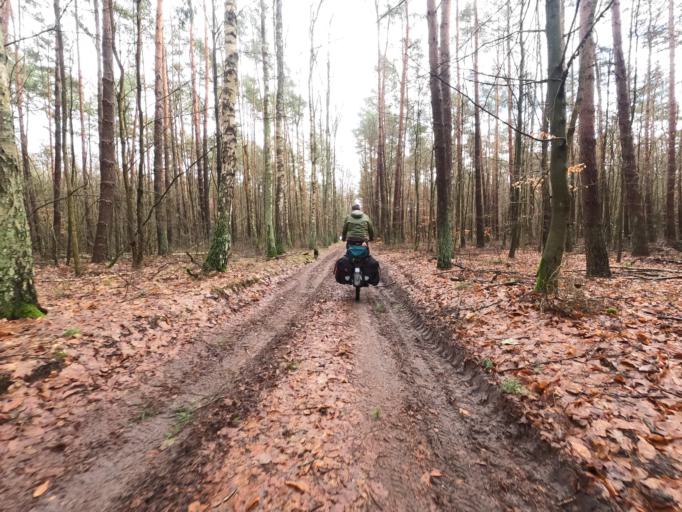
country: PL
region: Greater Poland Voivodeship
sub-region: Powiat pilski
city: Smilowo
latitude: 53.1131
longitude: 16.9290
